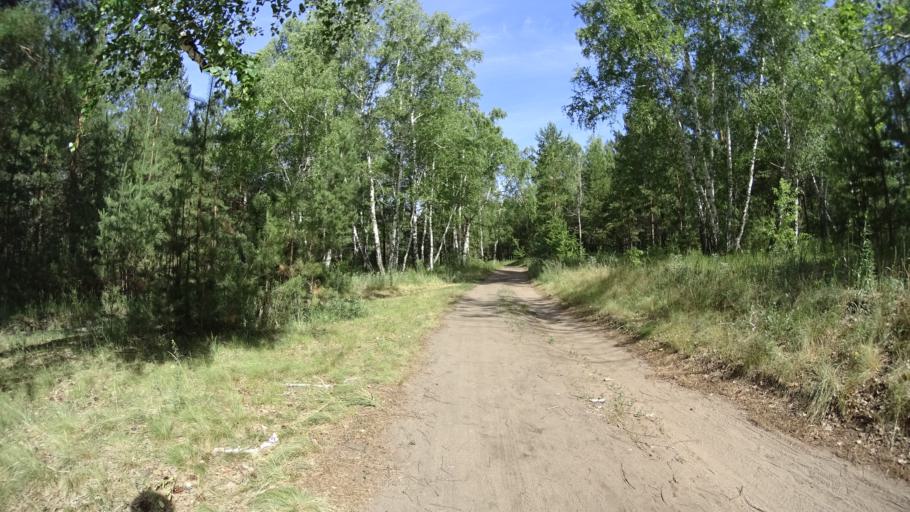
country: RU
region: Chelyabinsk
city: Troitsk
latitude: 54.0524
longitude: 61.6311
